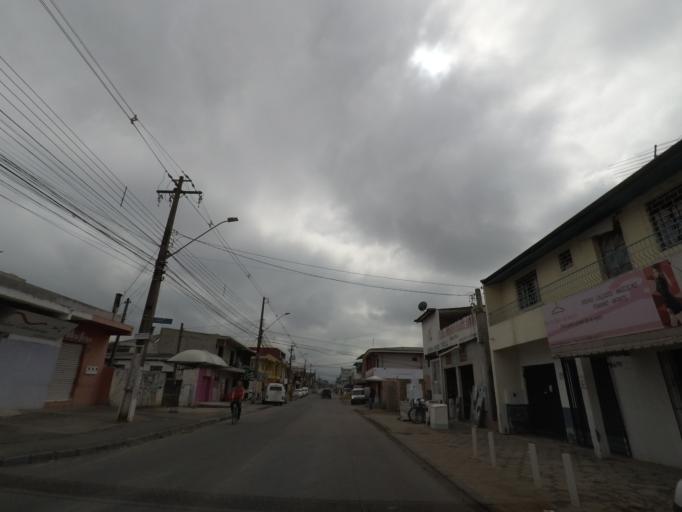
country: BR
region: Parana
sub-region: Curitiba
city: Curitiba
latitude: -25.5032
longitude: -49.3379
